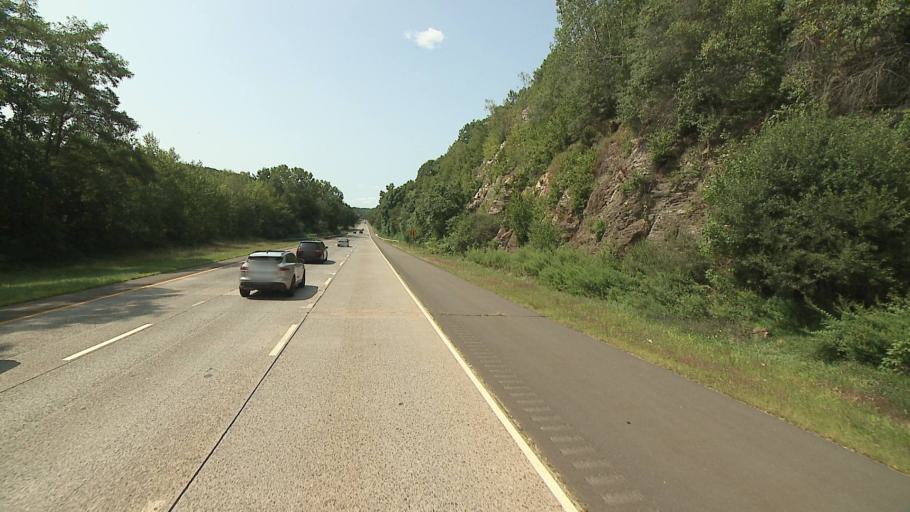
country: US
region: Connecticut
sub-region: Fairfield County
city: Trumbull
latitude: 41.2834
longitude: -73.2207
